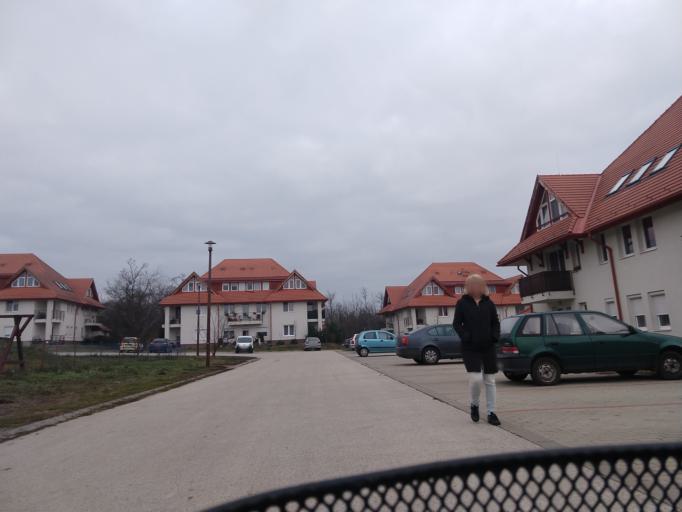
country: HU
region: Pest
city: Orbottyan
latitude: 47.6626
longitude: 19.2695
